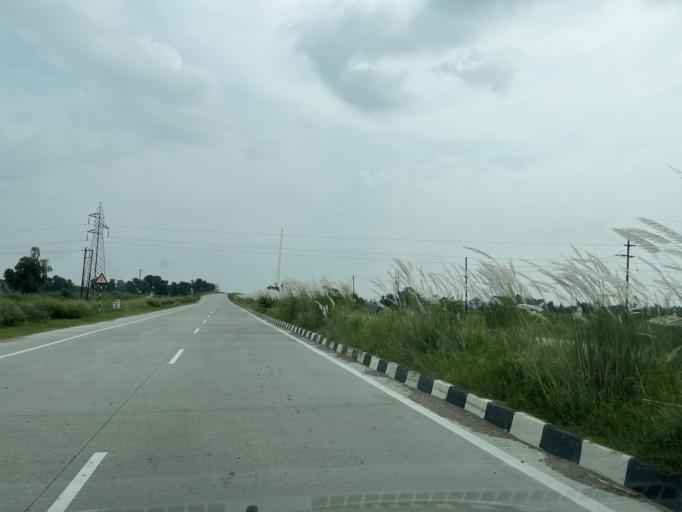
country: IN
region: Uttarakhand
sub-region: Udham Singh Nagar
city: Kashipur
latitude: 29.1939
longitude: 78.9370
